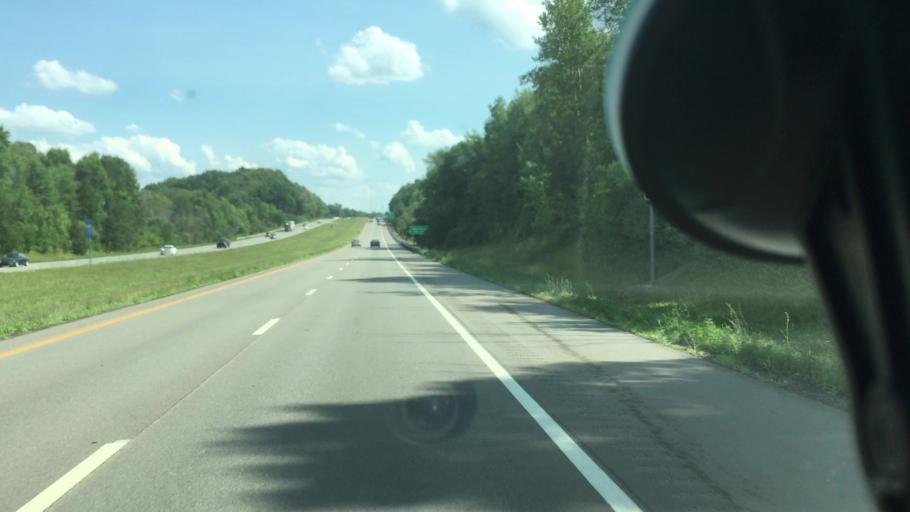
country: US
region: Ohio
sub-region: Mahoning County
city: Canfield
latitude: 41.0412
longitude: -80.7436
